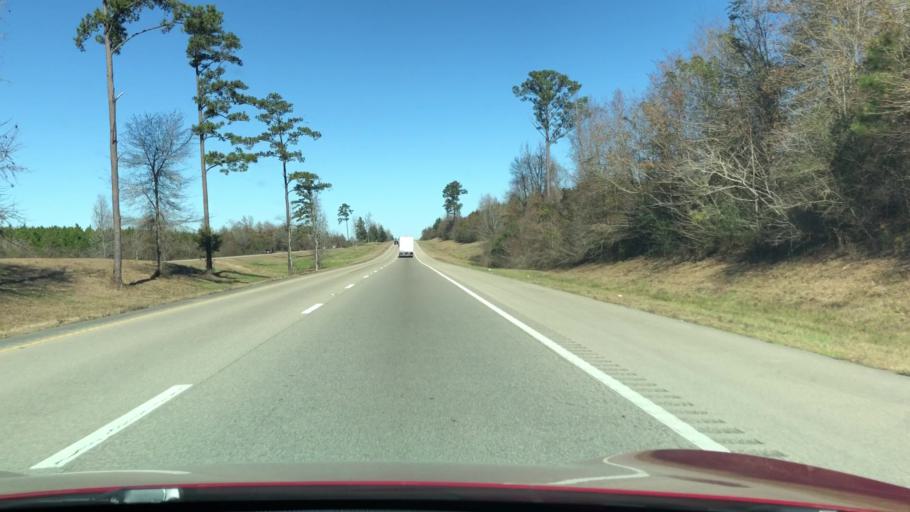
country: US
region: Mississippi
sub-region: Pearl River County
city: Poplarville
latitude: 30.7656
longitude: -89.5212
